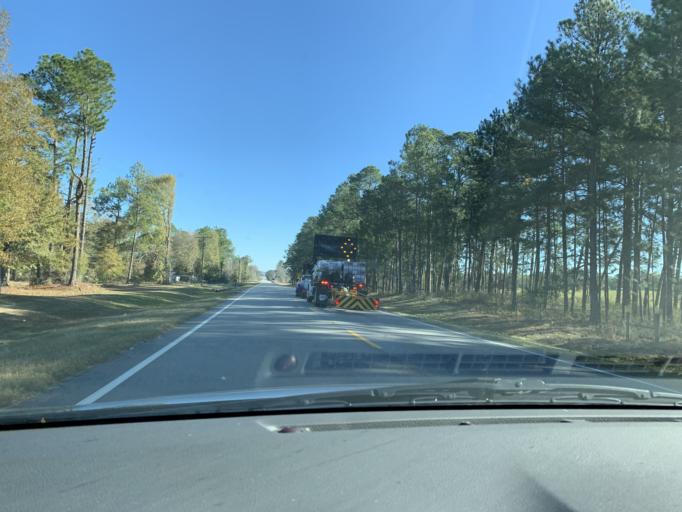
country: US
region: Georgia
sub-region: Ben Hill County
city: Fitzgerald
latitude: 31.7482
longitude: -83.1411
